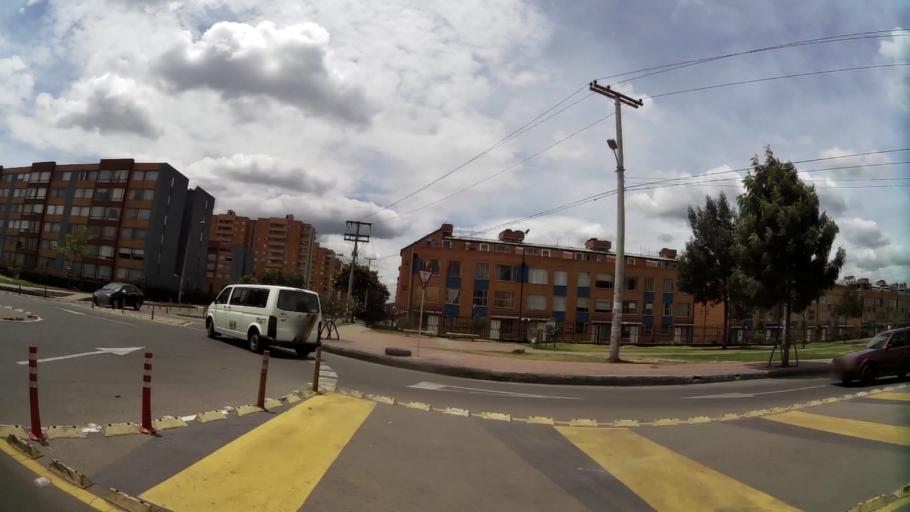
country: CO
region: Bogota D.C.
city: Bogota
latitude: 4.6379
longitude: -74.1523
